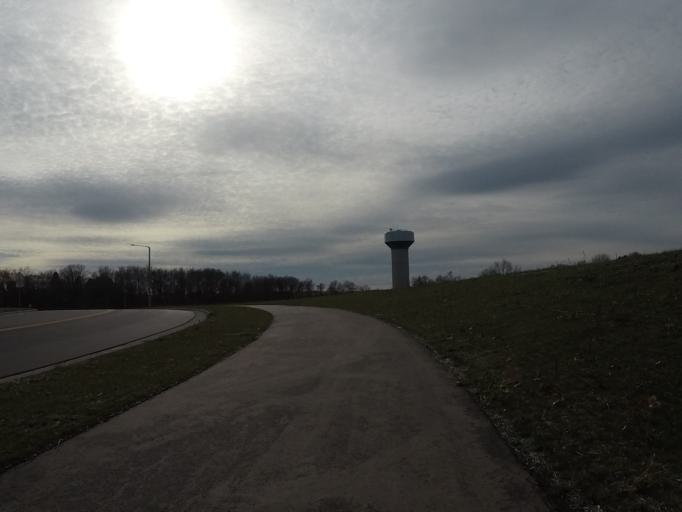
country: US
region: Wisconsin
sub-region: Dane County
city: Middleton
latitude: 43.0764
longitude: -89.5633
